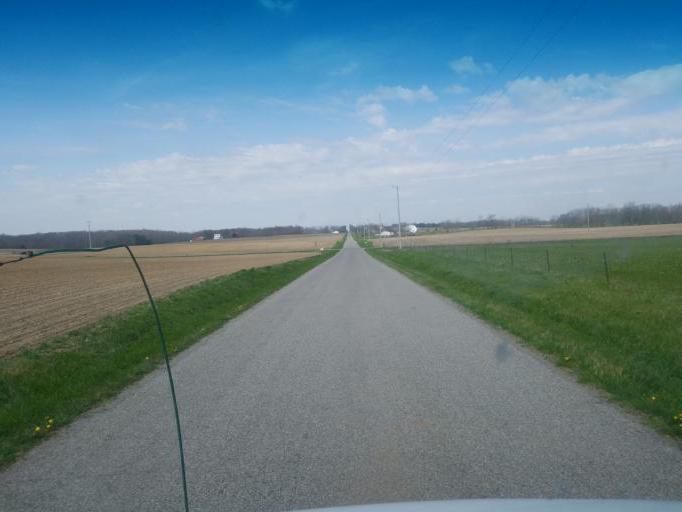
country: US
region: Ohio
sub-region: Logan County
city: Northwood
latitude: 40.4985
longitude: -83.6564
